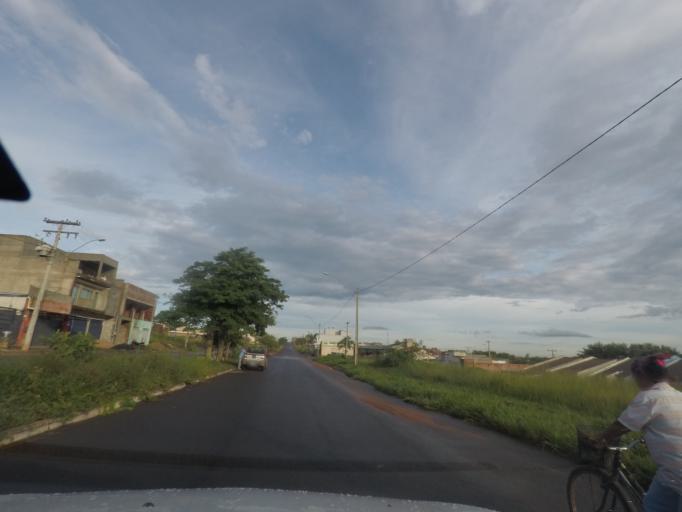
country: BR
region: Goias
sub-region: Goiania
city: Goiania
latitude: -16.7506
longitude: -49.3789
